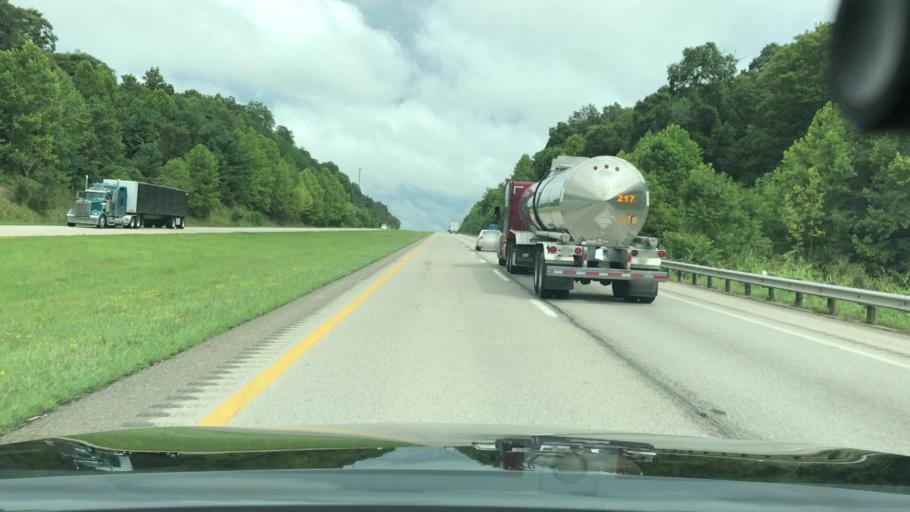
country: US
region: Ohio
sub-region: Gallia County
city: Gallipolis
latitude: 38.8908
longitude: -82.3563
